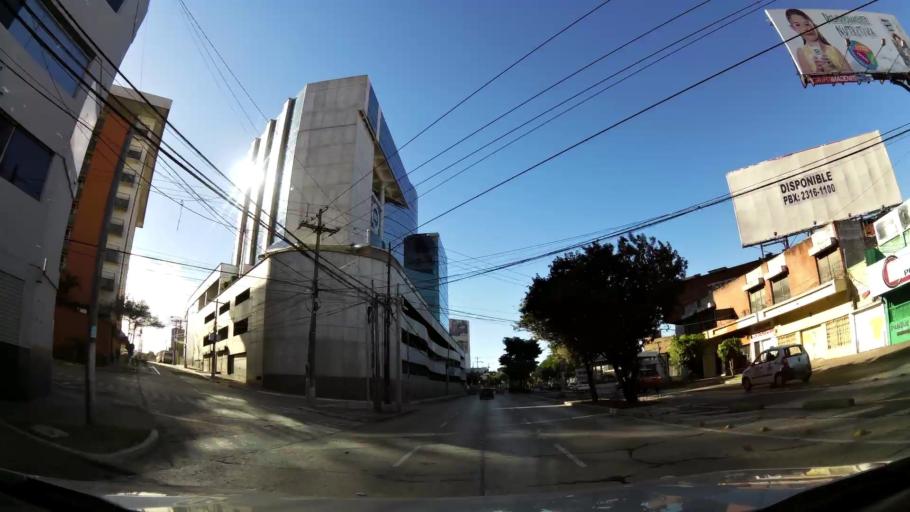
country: GT
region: Guatemala
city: Guatemala City
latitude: 14.6203
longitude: -90.5169
